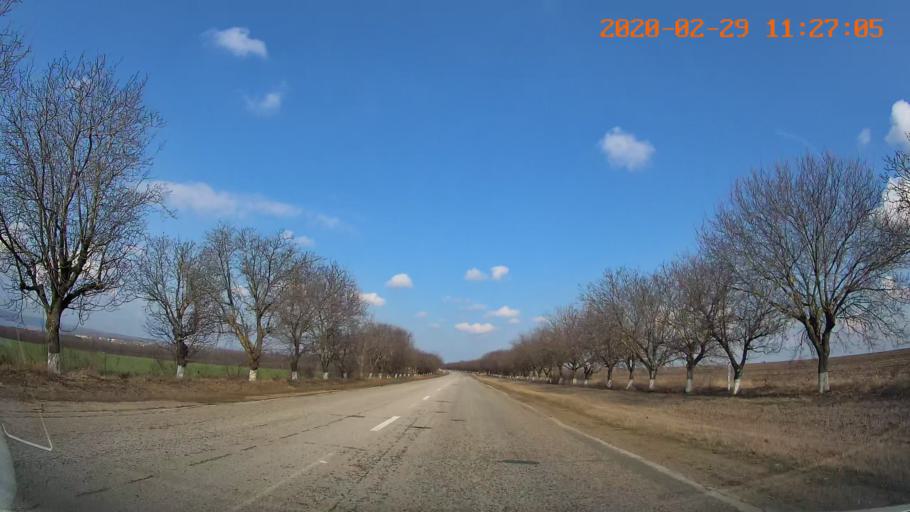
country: MD
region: Telenesti
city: Cocieri
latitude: 47.4628
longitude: 29.1437
